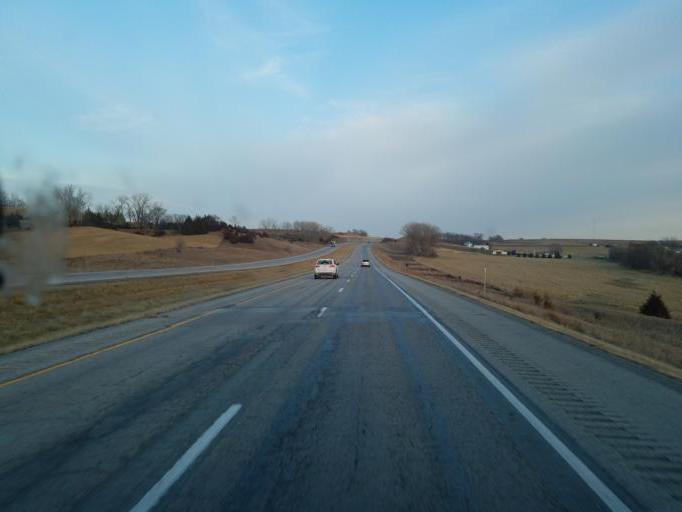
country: US
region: Iowa
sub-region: Harrison County
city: Missouri Valley
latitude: 41.4937
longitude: -95.8120
